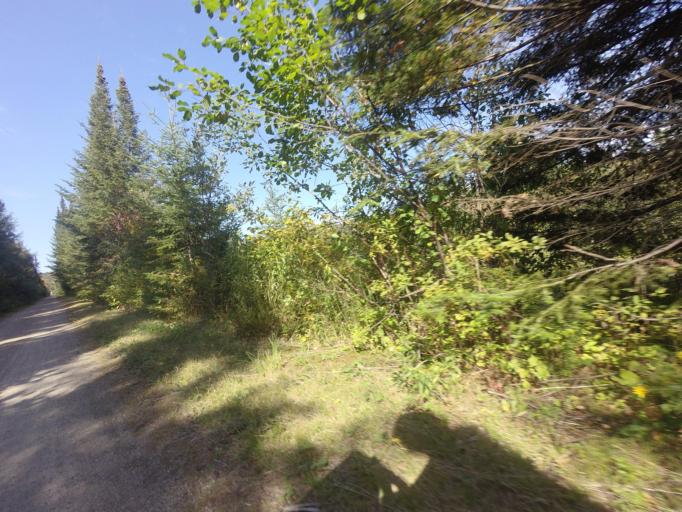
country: CA
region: Quebec
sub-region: Laurentides
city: Sainte-Agathe-des-Monts
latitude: 46.0634
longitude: -74.3047
